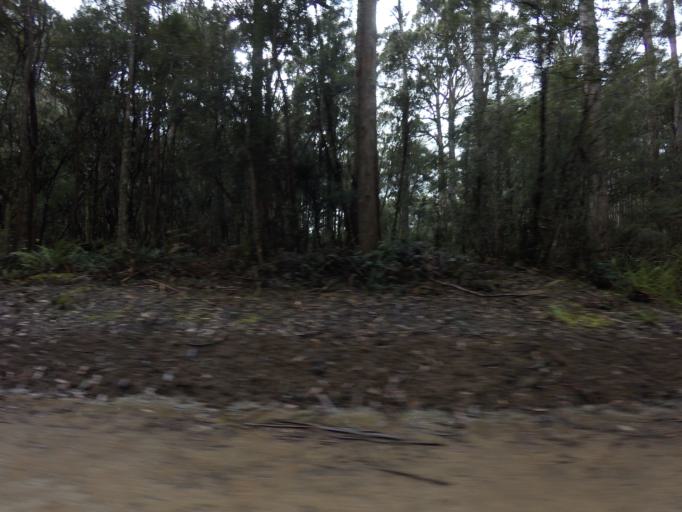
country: AU
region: Tasmania
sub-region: Huon Valley
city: Geeveston
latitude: -43.5602
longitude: 146.8909
